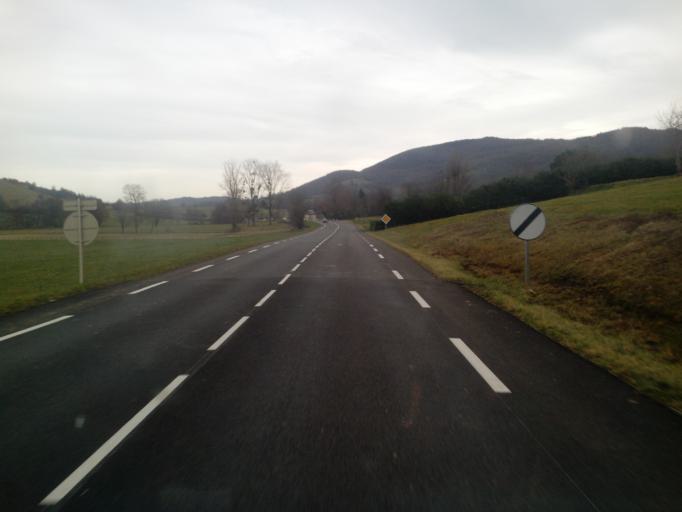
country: FR
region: Midi-Pyrenees
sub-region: Departement de l'Ariege
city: Foix
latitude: 43.0073
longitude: 1.4669
